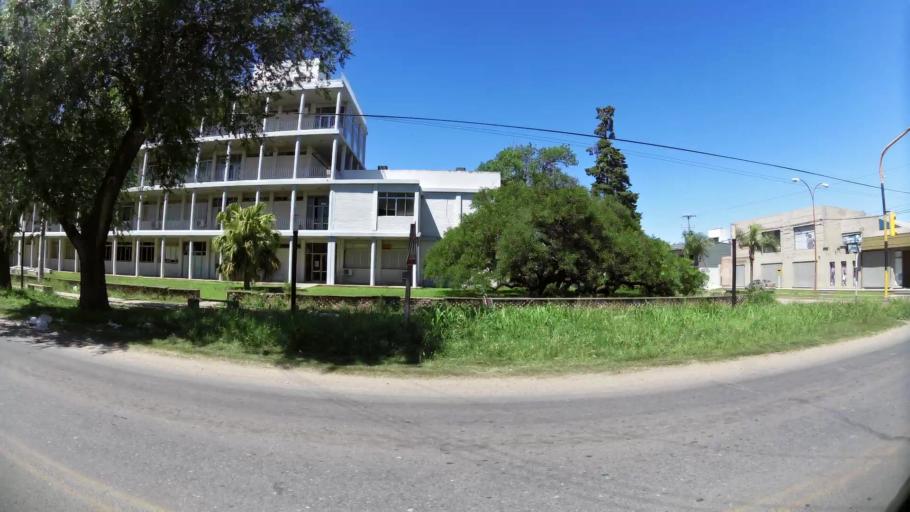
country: AR
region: Santa Fe
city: Esperanza
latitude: -31.4400
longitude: -60.9410
